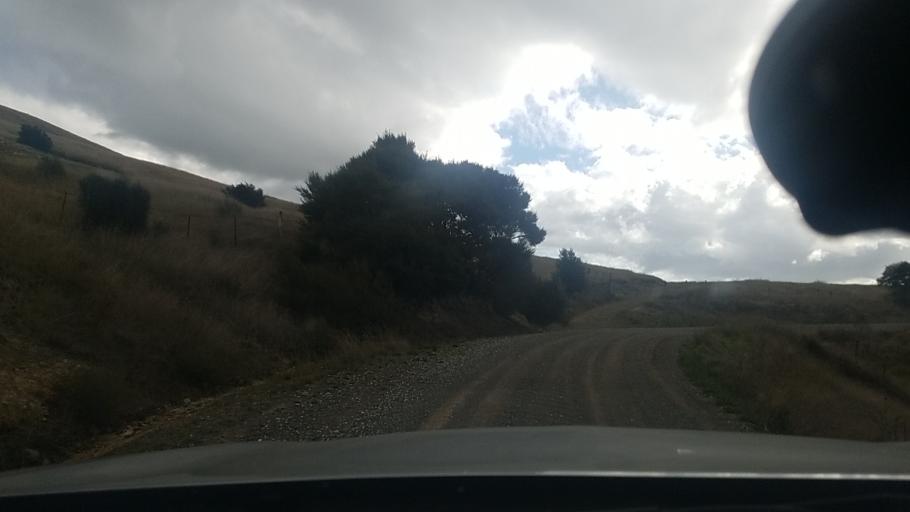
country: NZ
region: Marlborough
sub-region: Marlborough District
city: Blenheim
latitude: -41.5865
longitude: 174.0761
